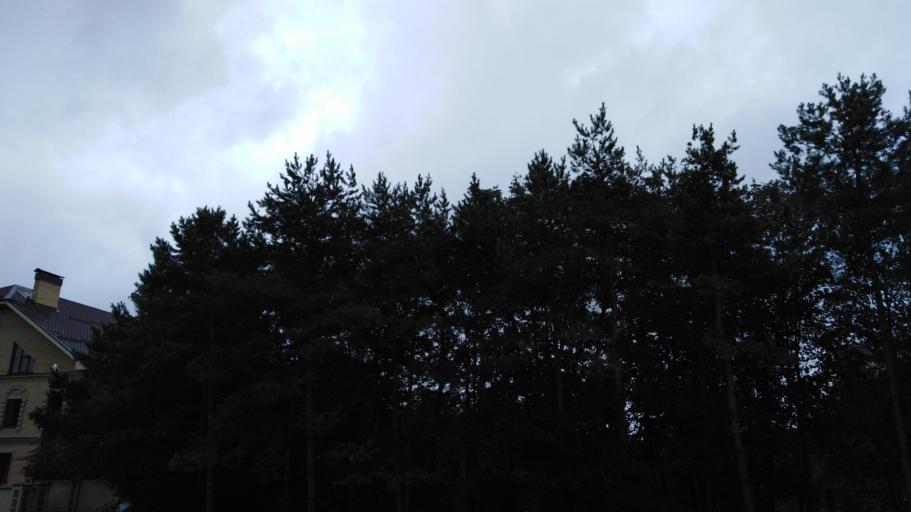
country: RU
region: Stavropol'skiy
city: Yessentukskaya
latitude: 44.0532
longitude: 42.9043
